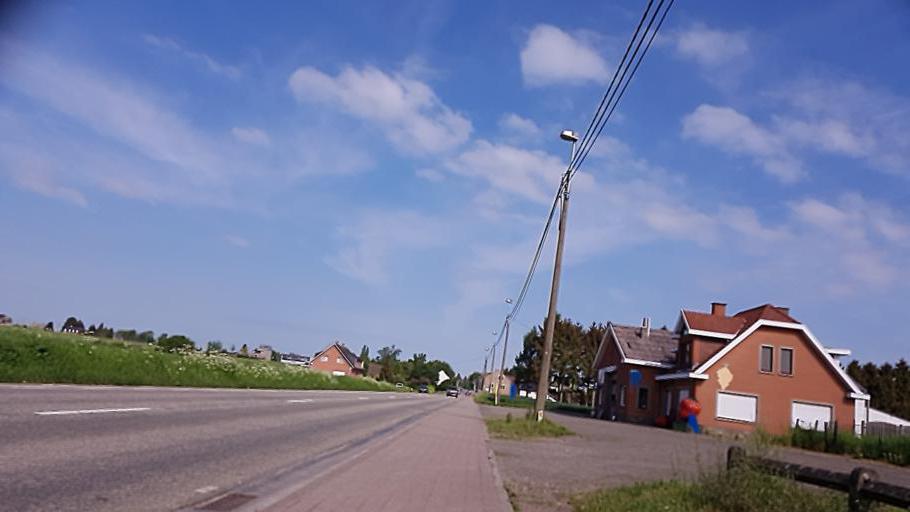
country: BE
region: Flanders
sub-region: Provincie Vlaams-Brabant
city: Overijse
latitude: 50.7622
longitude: 4.5575
